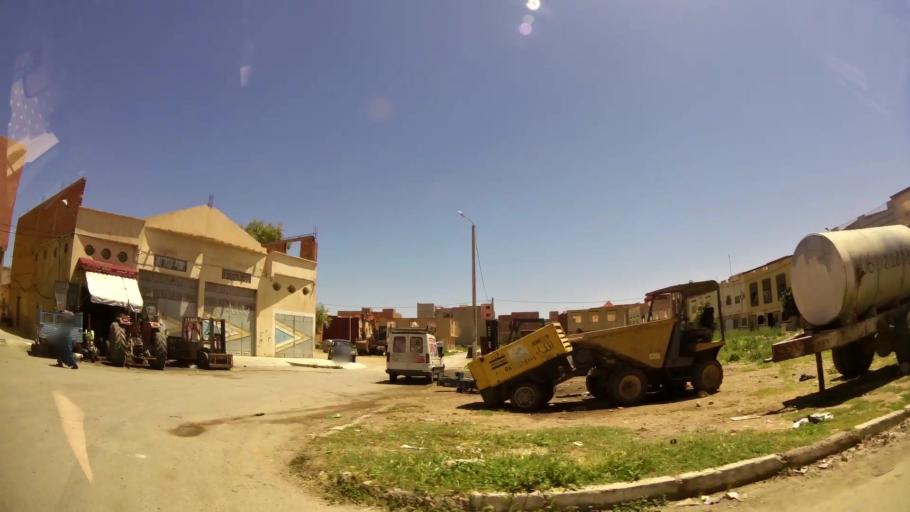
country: MA
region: Oriental
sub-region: Oujda-Angad
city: Oujda
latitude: 34.6750
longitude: -1.8847
